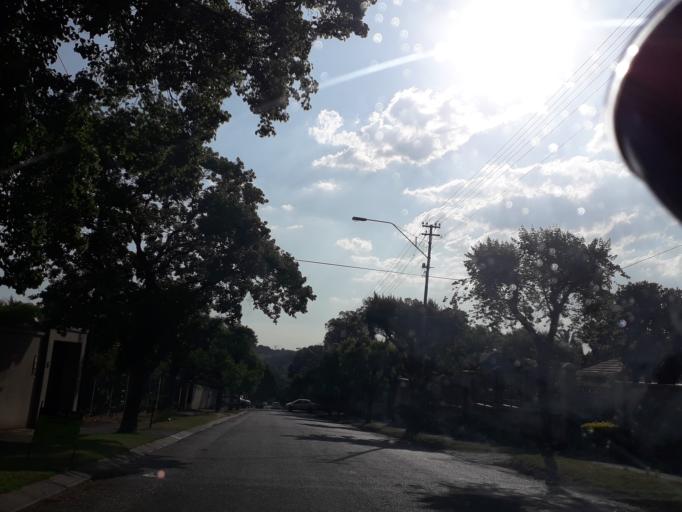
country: ZA
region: Gauteng
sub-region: City of Johannesburg Metropolitan Municipality
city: Johannesburg
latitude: -26.1441
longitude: 28.0779
